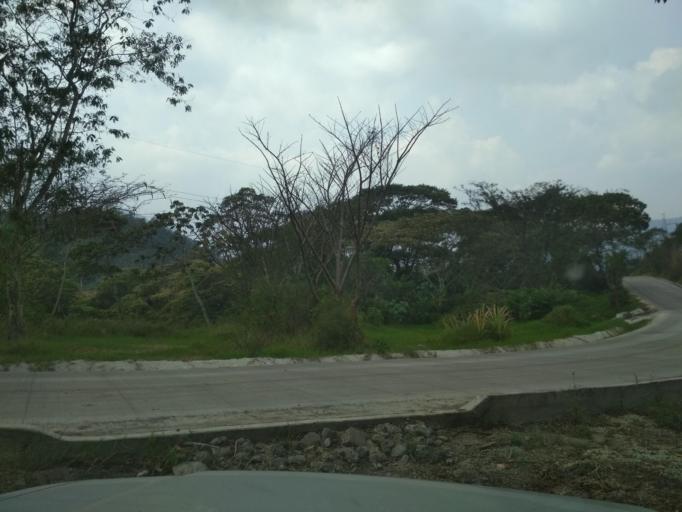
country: MX
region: Veracruz
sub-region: Cordoba
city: San Jose de Tapia
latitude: 18.8337
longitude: -96.9750
